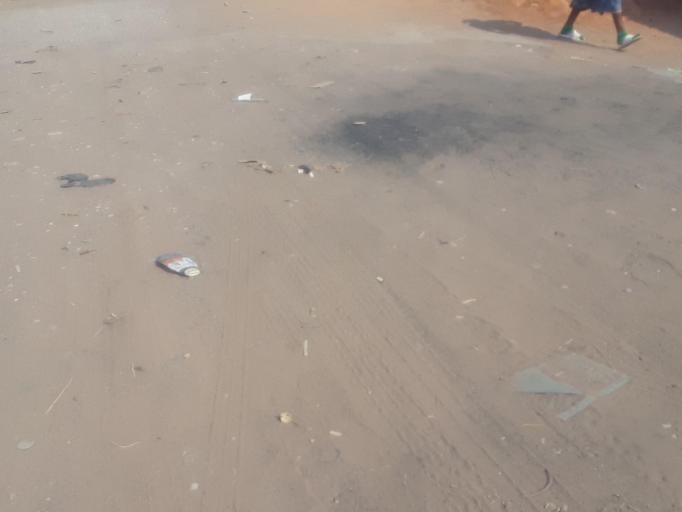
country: ZM
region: Lusaka
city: Lusaka
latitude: -15.3536
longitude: 28.2920
